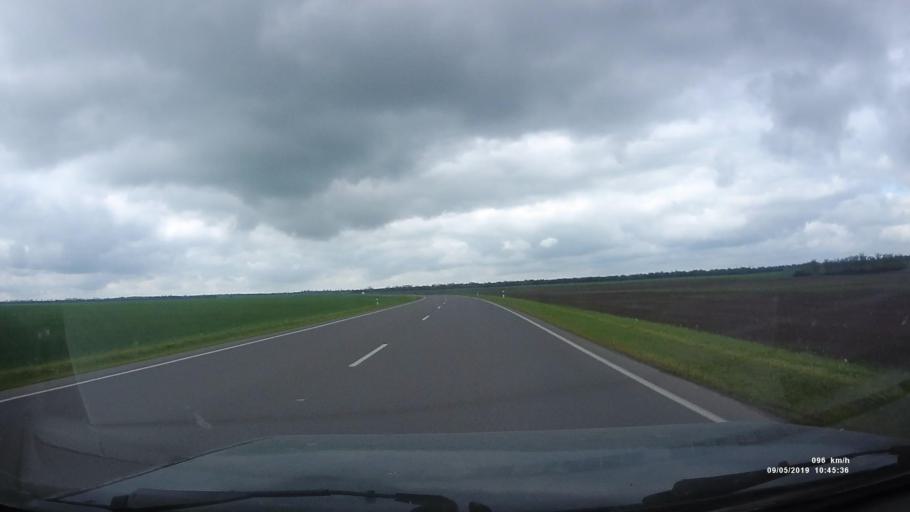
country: RU
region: Rostov
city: Peshkovo
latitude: 46.9941
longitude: 39.3650
